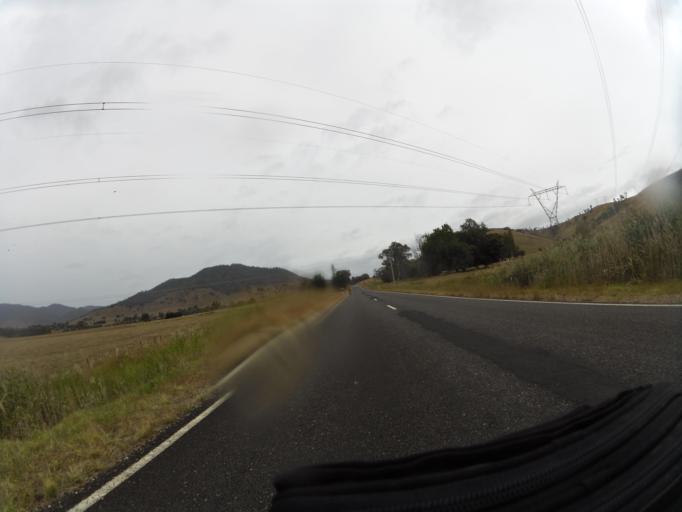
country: AU
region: New South Wales
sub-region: Greater Hume Shire
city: Holbrook
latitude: -36.2101
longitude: 147.7335
